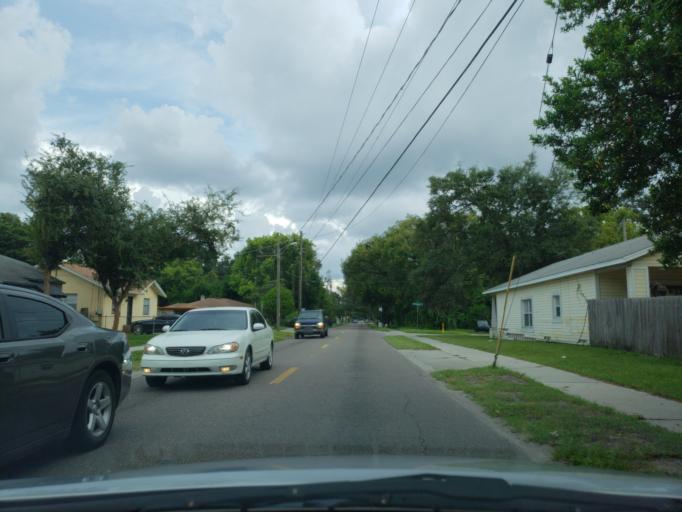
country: US
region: Florida
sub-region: Hillsborough County
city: Tampa
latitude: 27.9948
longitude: -82.4430
